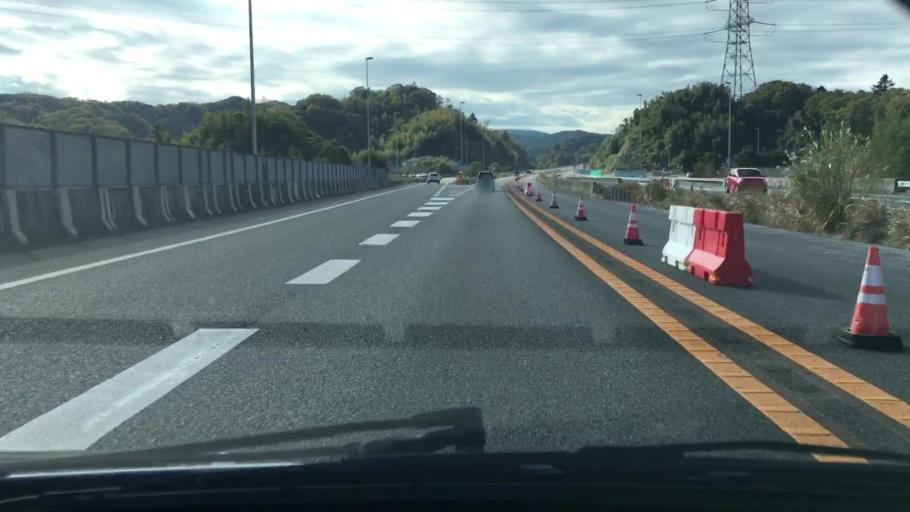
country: JP
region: Chiba
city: Kimitsu
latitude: 35.2854
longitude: 139.9276
